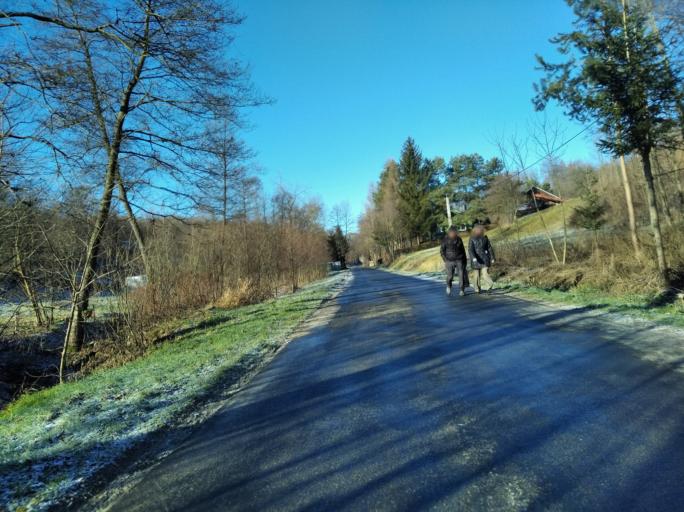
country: PL
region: Subcarpathian Voivodeship
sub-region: Powiat strzyzowski
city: Czudec
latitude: 49.9513
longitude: 21.7761
